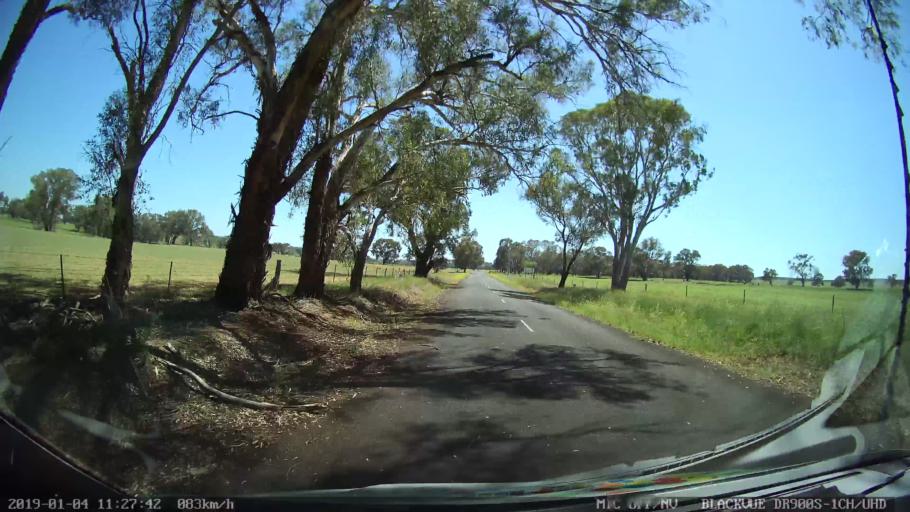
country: AU
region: New South Wales
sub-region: Cabonne
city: Molong
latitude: -33.1070
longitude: 148.7654
